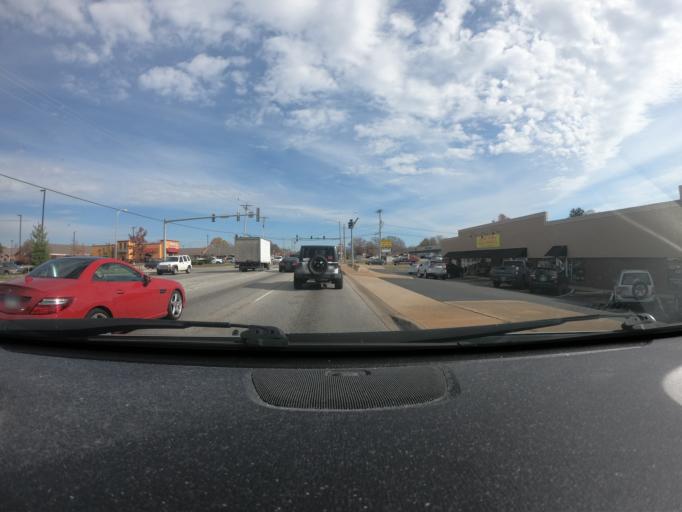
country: US
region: Arkansas
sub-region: Benton County
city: Rogers
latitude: 36.3341
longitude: -94.1497
